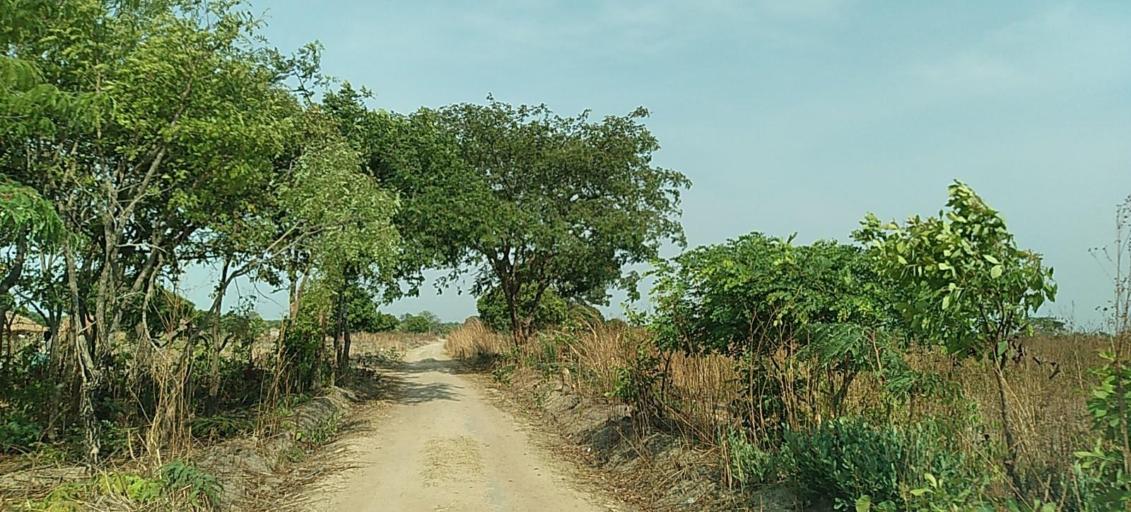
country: ZM
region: Copperbelt
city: Luanshya
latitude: -13.2178
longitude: 28.6525
